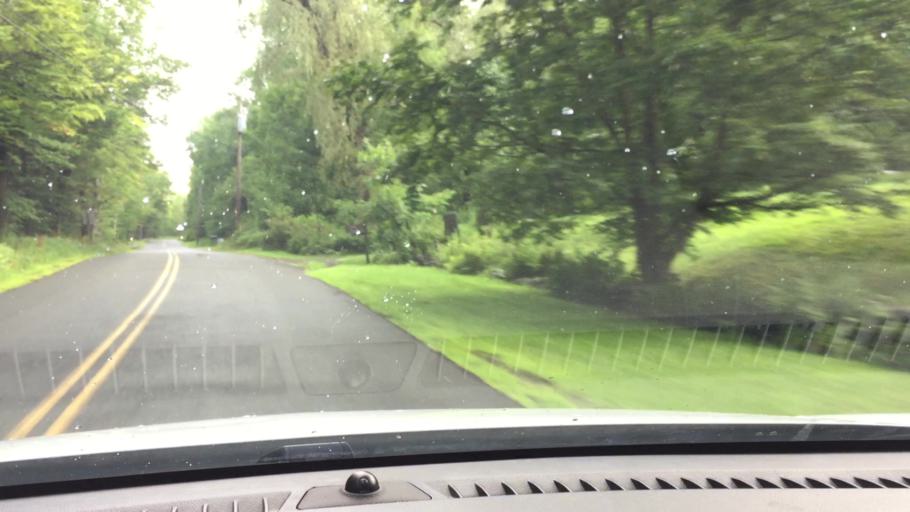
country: US
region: Massachusetts
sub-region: Berkshire County
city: Becket
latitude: 42.4193
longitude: -72.9843
